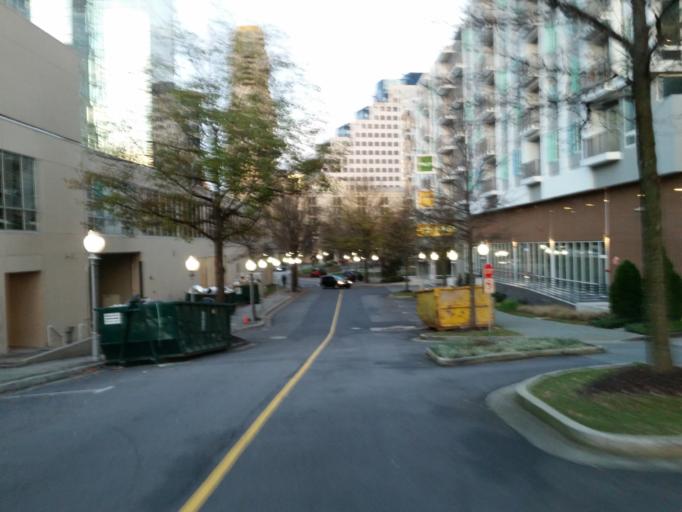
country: US
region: Georgia
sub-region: DeKalb County
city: North Atlanta
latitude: 33.8464
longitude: -84.3719
